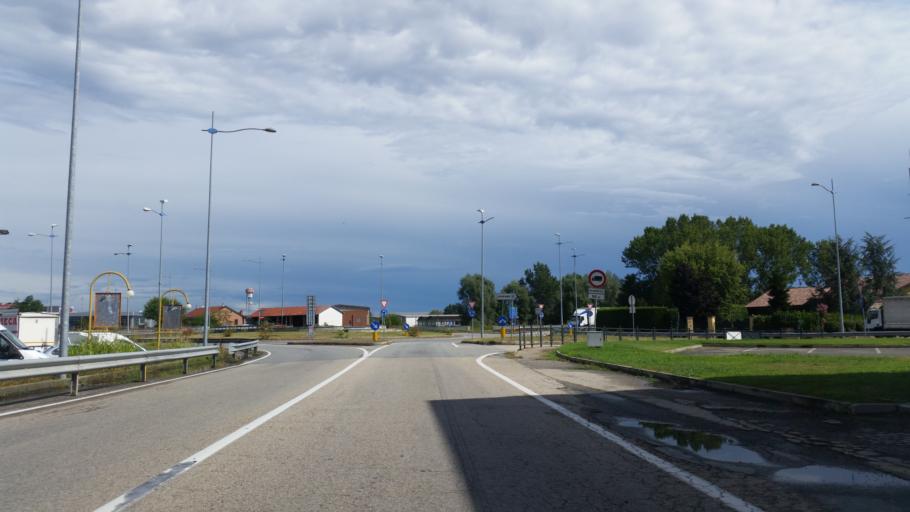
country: IT
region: Piedmont
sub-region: Provincia di Torino
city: Poirino
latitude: 44.9236
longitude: 7.8381
